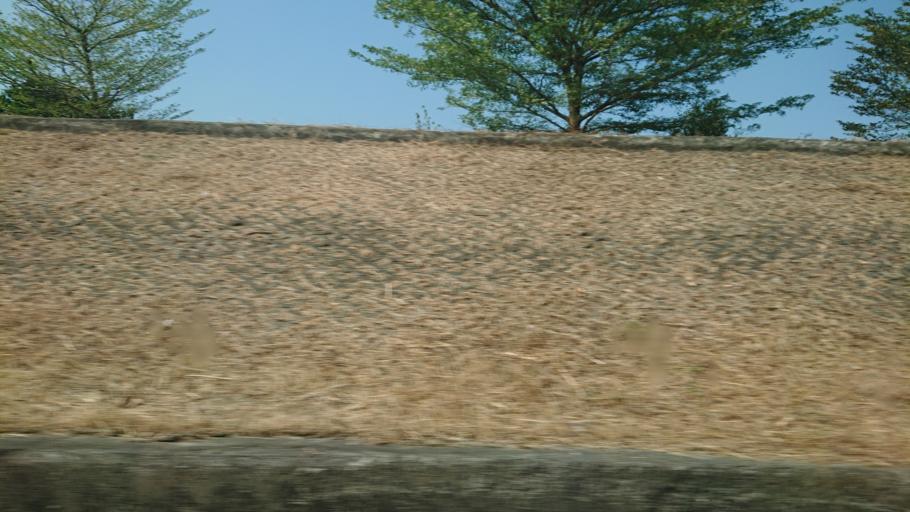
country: TW
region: Taiwan
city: Lugu
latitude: 23.7561
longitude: 120.6590
